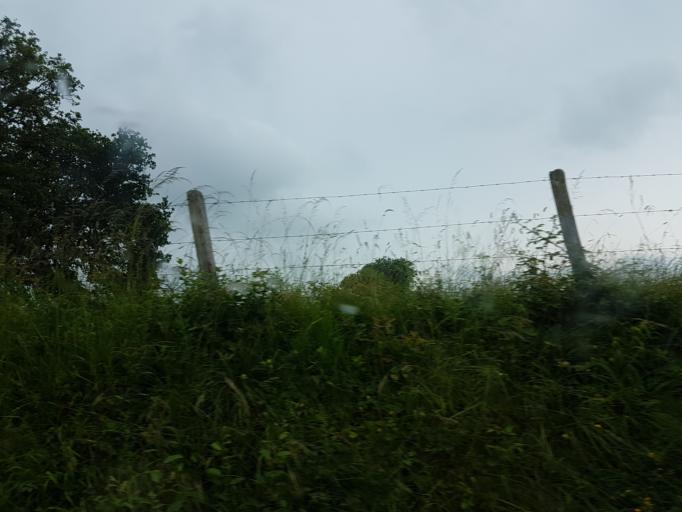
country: FR
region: Bourgogne
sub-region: Departement de la Nievre
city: Corbigny
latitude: 47.2166
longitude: 3.7106
